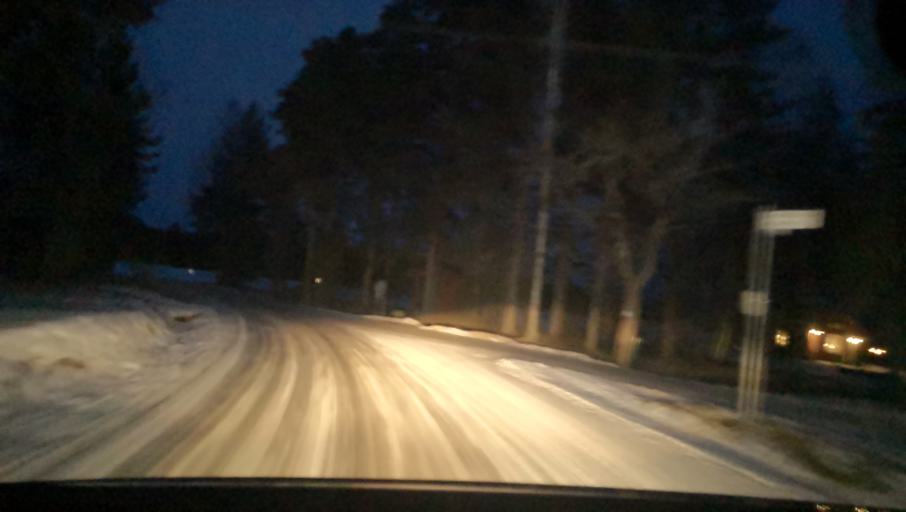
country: SE
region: Uppsala
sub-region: Heby Kommun
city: Tarnsjo
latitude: 60.2623
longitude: 16.7927
